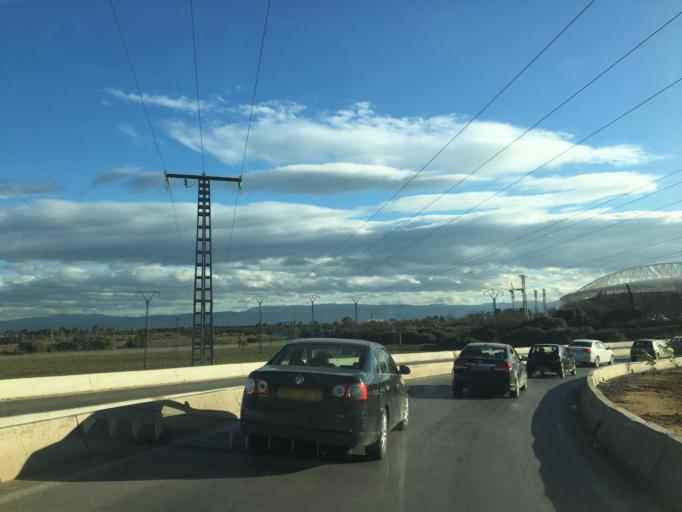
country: DZ
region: Tipaza
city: Baraki
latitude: 36.6992
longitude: 3.1220
